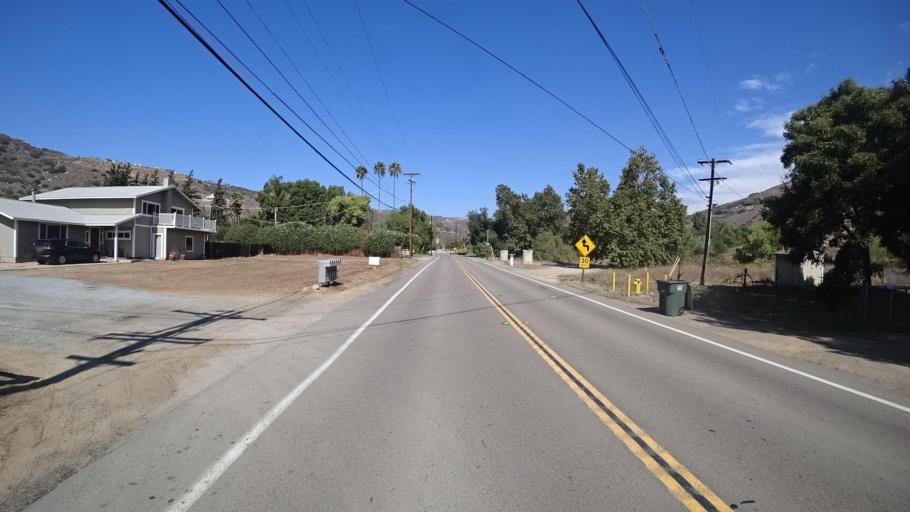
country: US
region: California
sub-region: San Diego County
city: Crest
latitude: 32.7961
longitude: -116.8461
